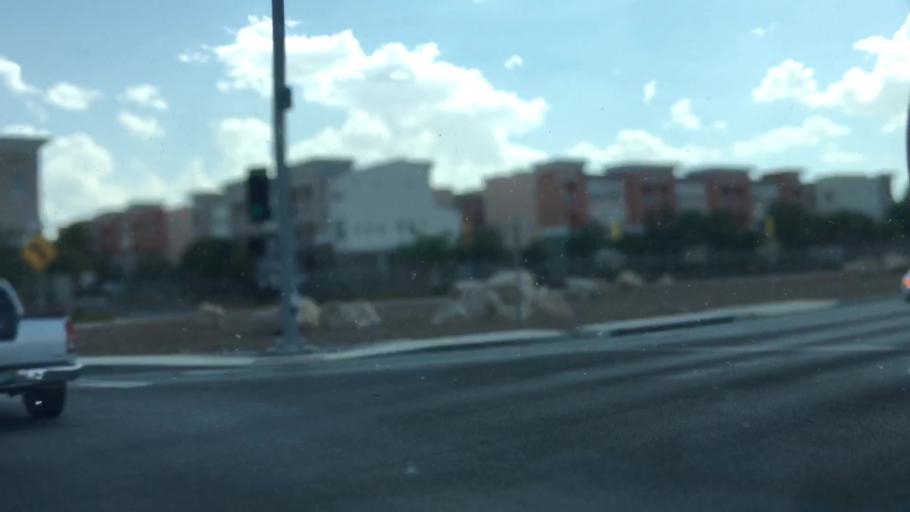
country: US
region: Nevada
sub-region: Clark County
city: Whitney
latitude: 36.0713
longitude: -115.0405
